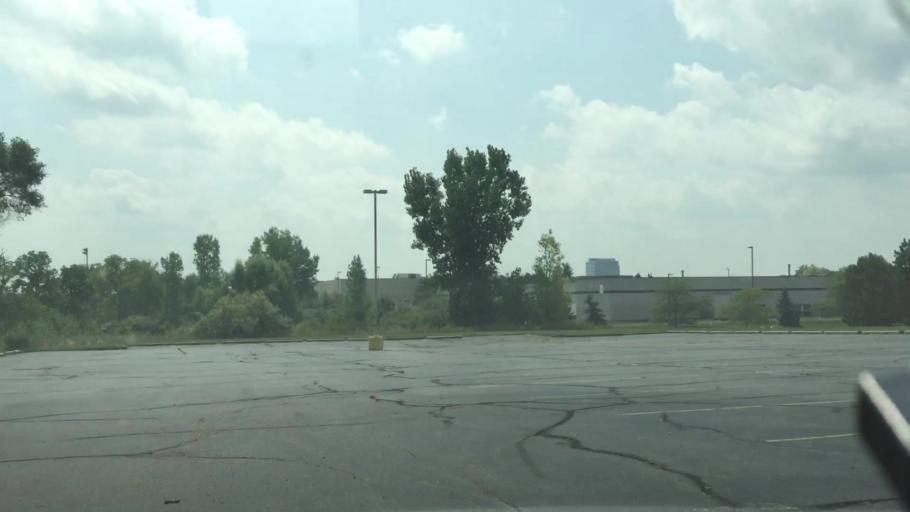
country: US
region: Michigan
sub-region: Oakland County
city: Auburn Hills
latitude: 42.6698
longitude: -83.2252
